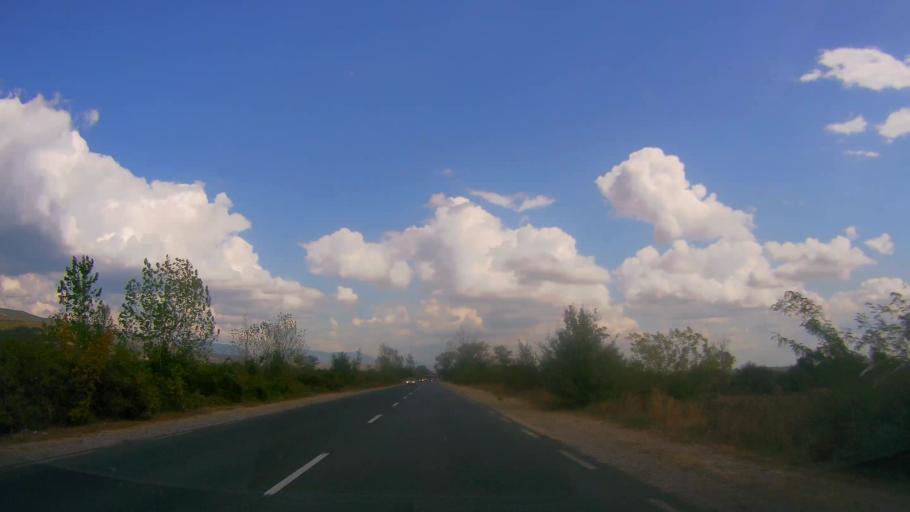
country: BG
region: Sliven
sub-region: Obshtina Sliven
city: Sliven
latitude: 42.6339
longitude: 26.2068
